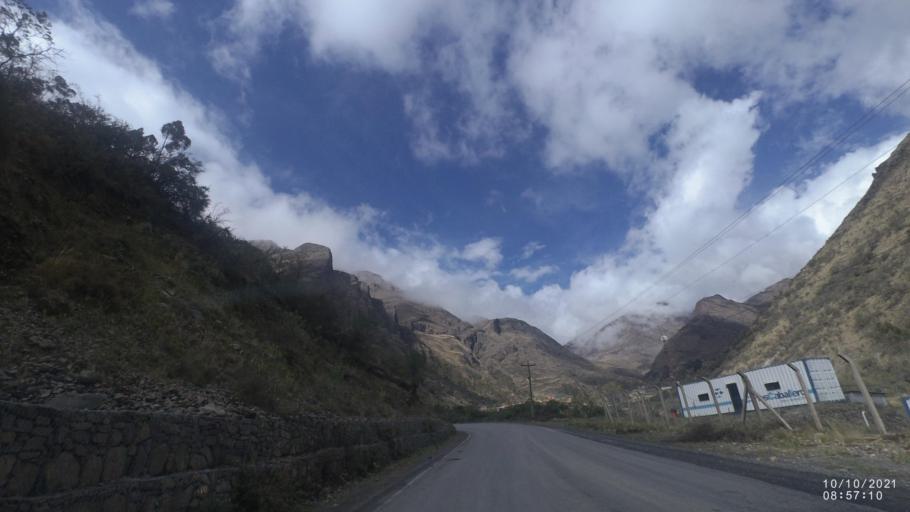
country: BO
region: La Paz
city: Quime
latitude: -16.9930
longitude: -67.2489
